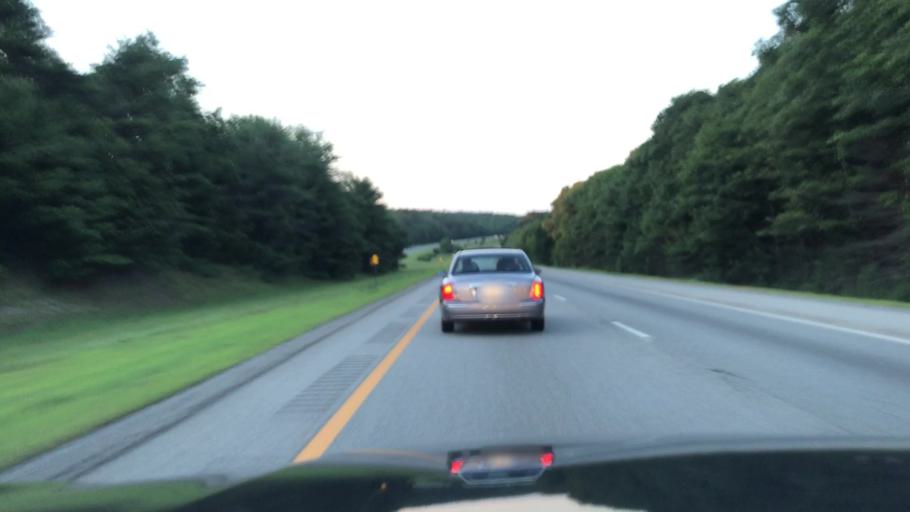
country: US
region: Rhode Island
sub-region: Kent County
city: West Greenwich
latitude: 41.6239
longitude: -71.6409
